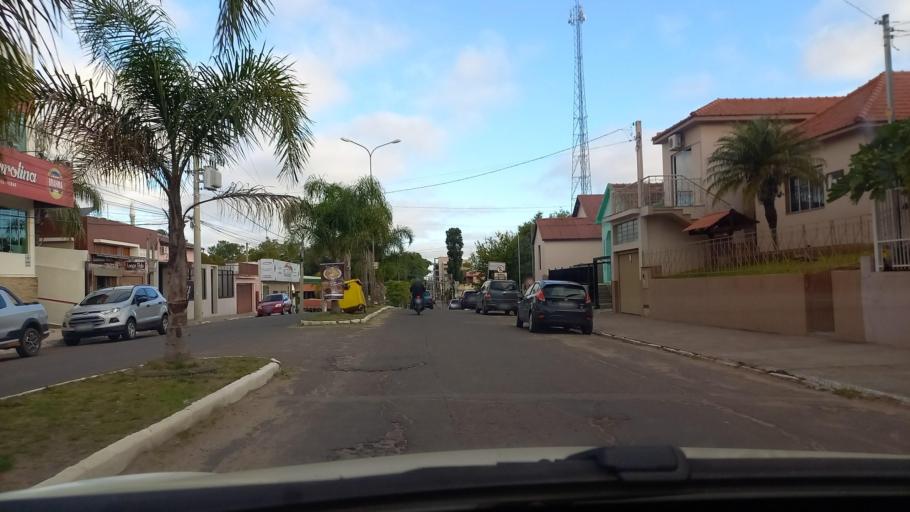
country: BR
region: Rio Grande do Sul
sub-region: Rosario Do Sul
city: Rosario do Sul
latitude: -30.2495
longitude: -54.9201
